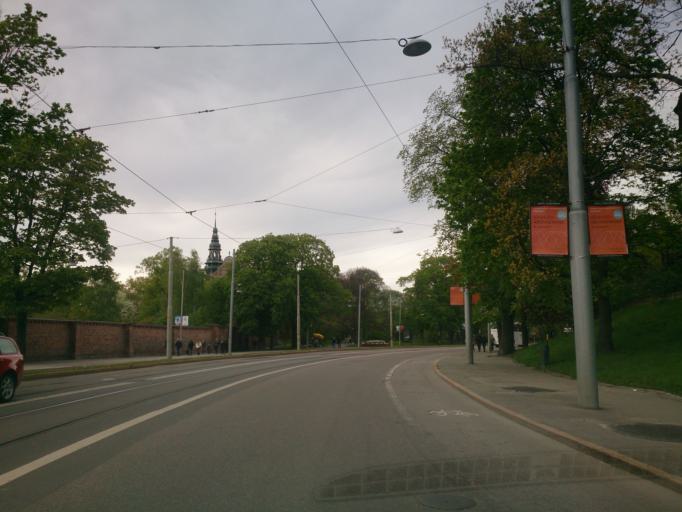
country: SE
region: Stockholm
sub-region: Stockholms Kommun
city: OEstermalm
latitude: 59.3263
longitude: 18.0964
